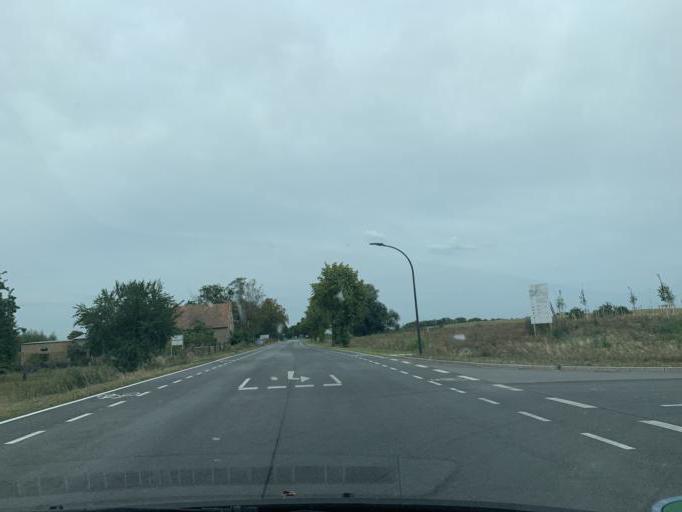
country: DE
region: Brandenburg
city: Gransee
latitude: 53.0033
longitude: 13.1749
